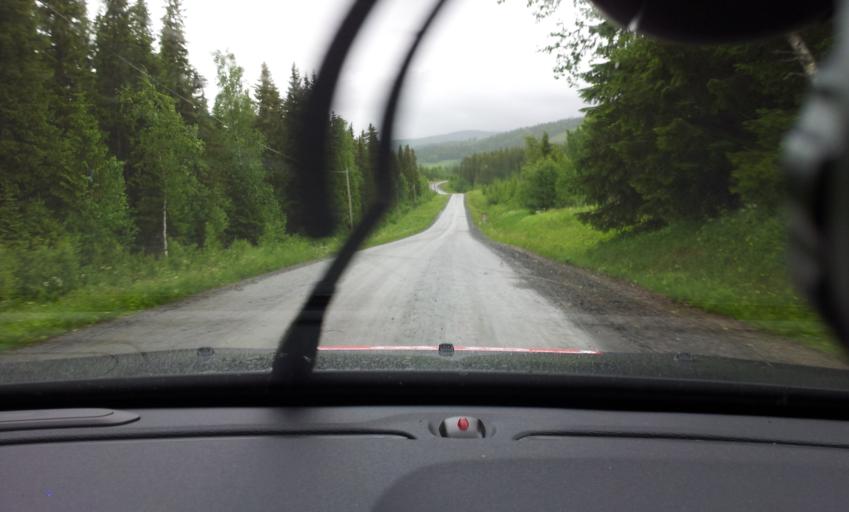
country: SE
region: Jaemtland
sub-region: Are Kommun
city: Are
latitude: 63.4463
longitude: 12.8037
